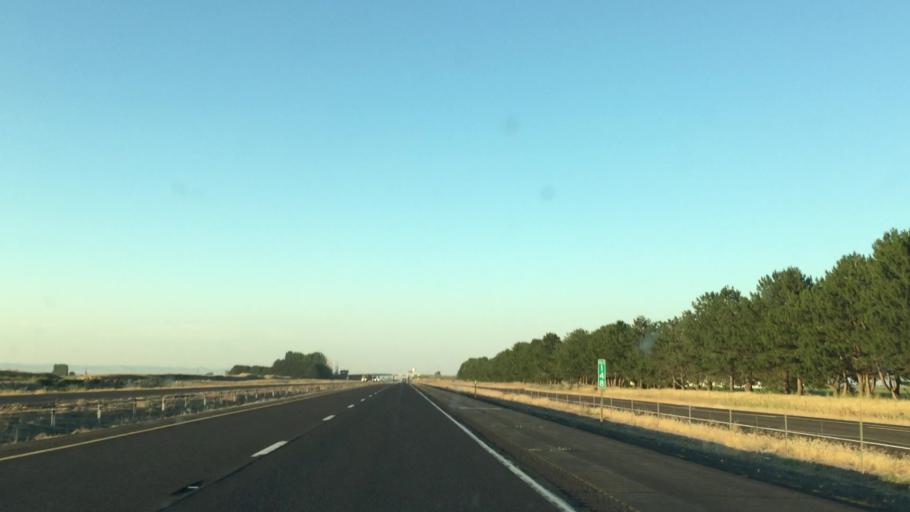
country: US
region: Washington
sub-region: Grant County
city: Quincy
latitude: 47.0650
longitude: -119.8849
